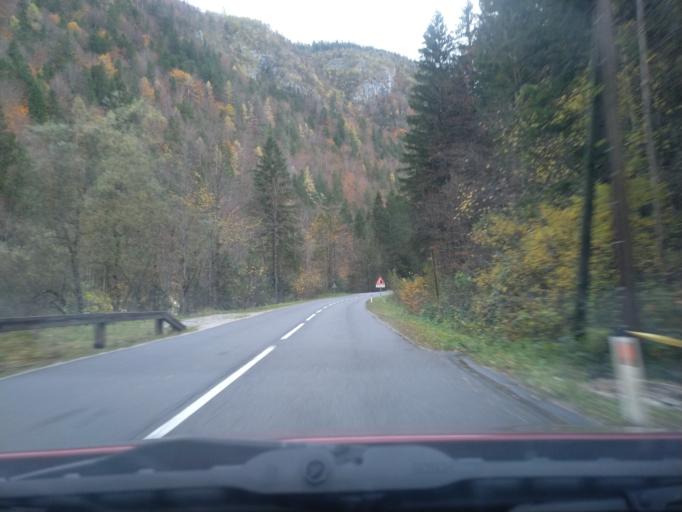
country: SI
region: Luce
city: Luce
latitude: 46.3667
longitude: 14.7313
